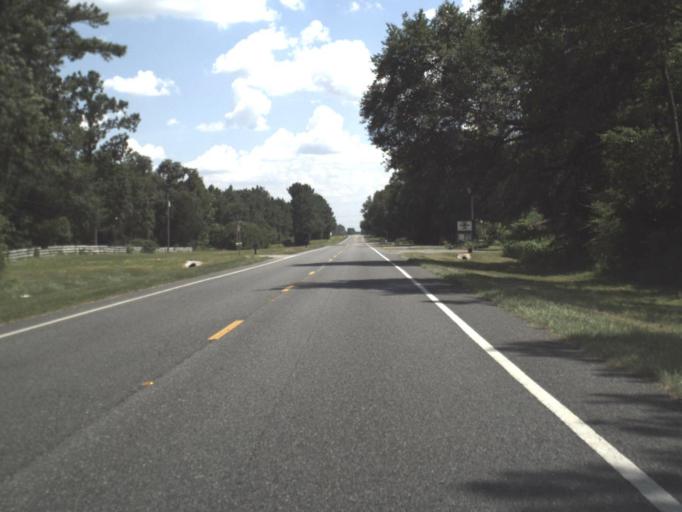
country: US
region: Florida
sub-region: Alachua County
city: High Springs
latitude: 29.9603
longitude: -82.6038
